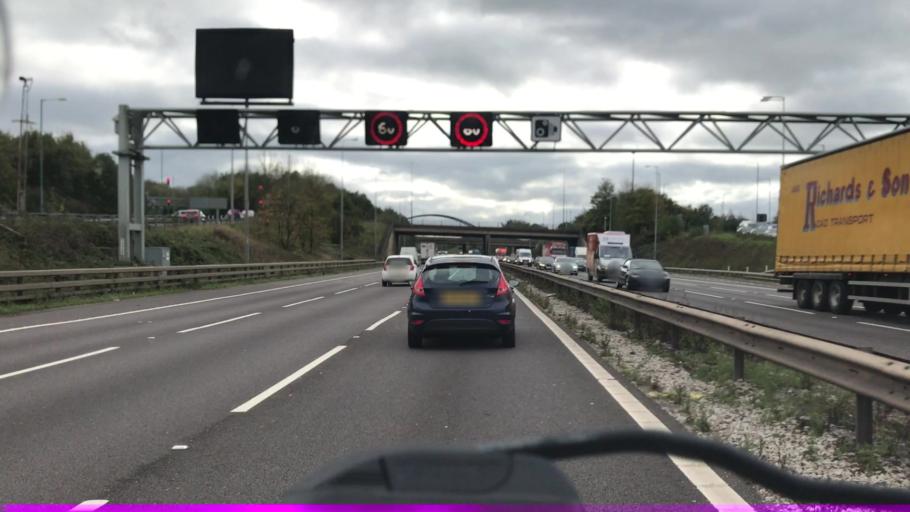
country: GB
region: England
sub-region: Solihull
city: Cheswick Green
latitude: 52.3816
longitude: -1.7849
